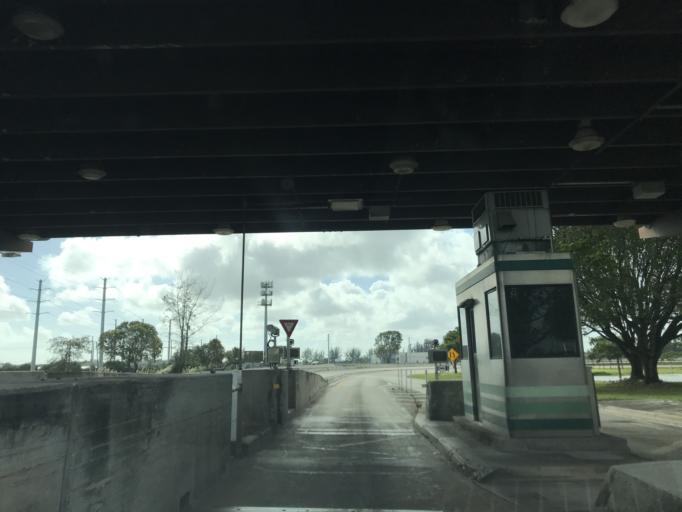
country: US
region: Florida
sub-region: Broward County
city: Coconut Creek
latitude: 26.2725
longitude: -80.1659
